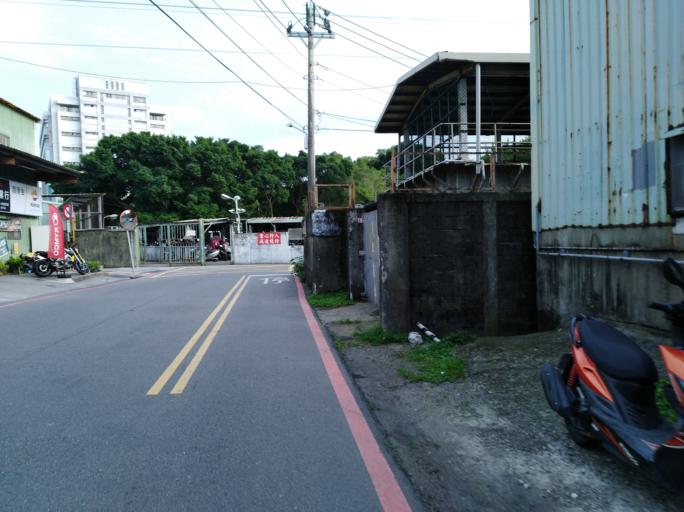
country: TW
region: Taipei
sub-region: Taipei
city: Banqiao
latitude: 25.0363
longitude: 121.4283
